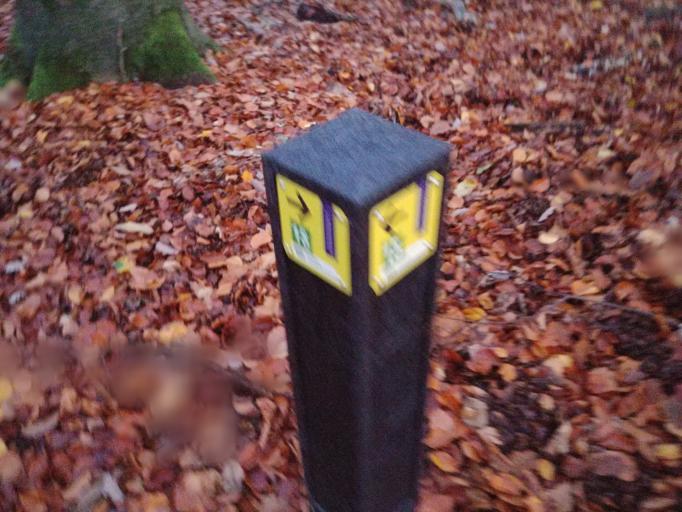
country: NL
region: Gelderland
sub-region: Gemeente Rheden
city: De Steeg
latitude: 52.0284
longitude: 6.0434
